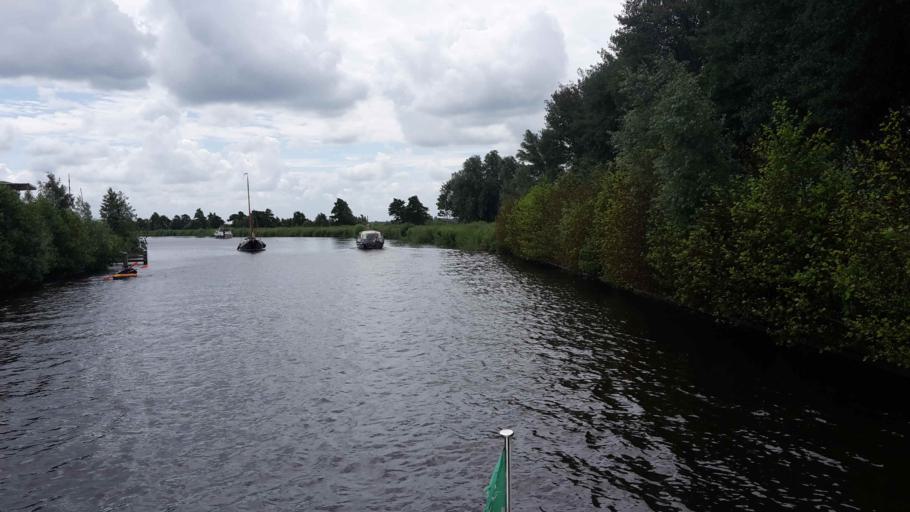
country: NL
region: Overijssel
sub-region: Gemeente Steenwijkerland
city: Giethoorn
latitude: 52.7091
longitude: 6.0726
